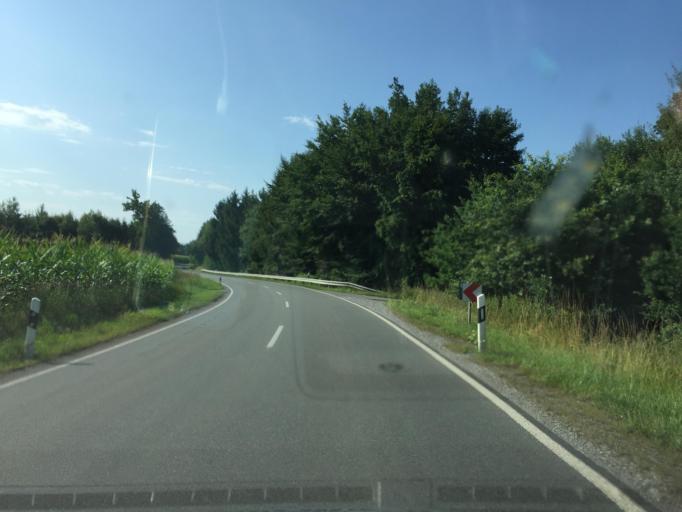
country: DE
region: Bavaria
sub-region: Upper Bavaria
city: Tuntenhausen
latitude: 47.9160
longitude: 11.9873
